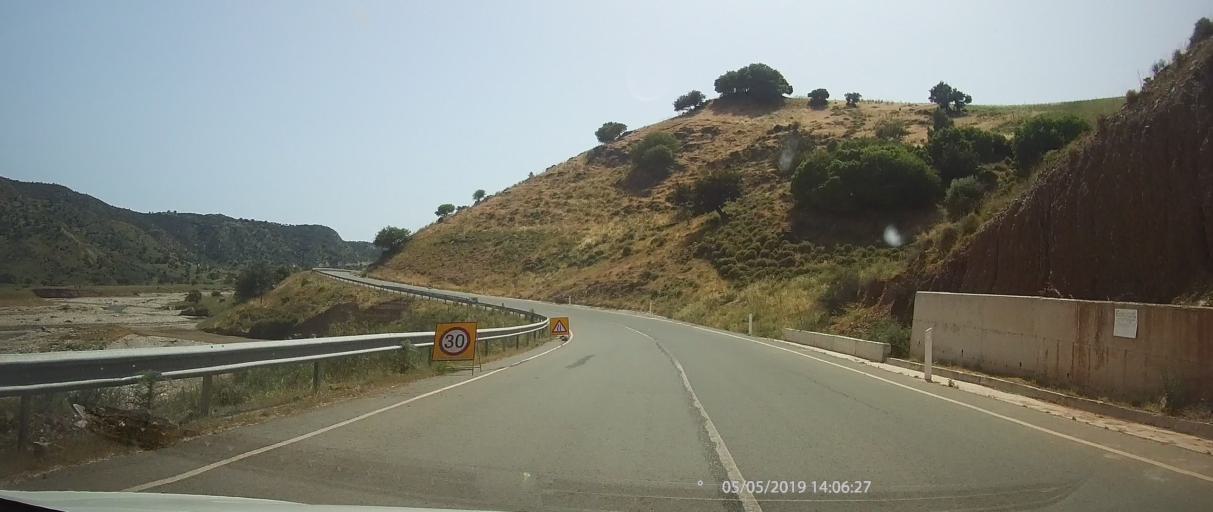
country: CY
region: Limassol
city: Pissouri
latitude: 34.7445
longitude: 32.6067
